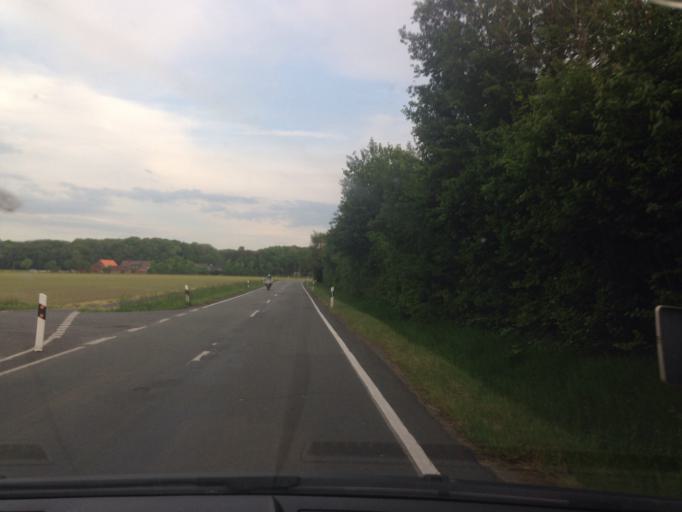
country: DE
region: North Rhine-Westphalia
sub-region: Regierungsbezirk Munster
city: Greven
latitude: 52.0284
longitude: 7.5605
